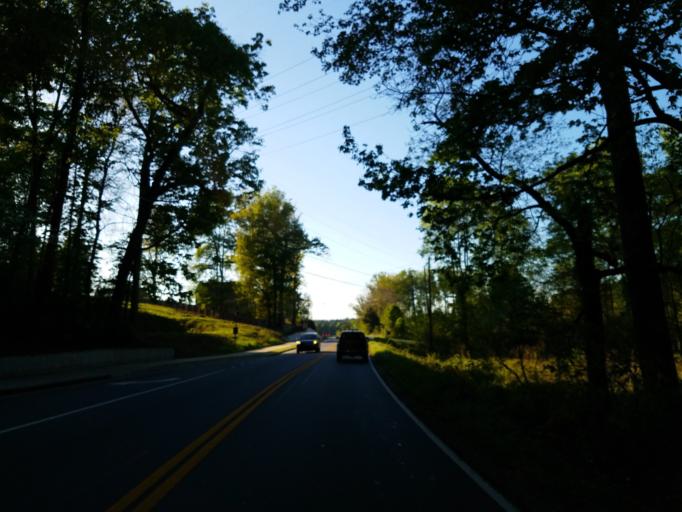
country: US
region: Georgia
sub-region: Cobb County
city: Kennesaw
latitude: 33.9894
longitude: -84.5930
